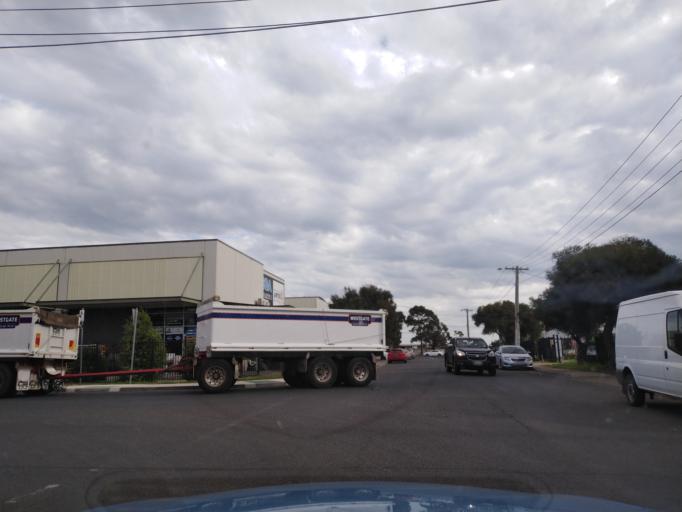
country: AU
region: Victoria
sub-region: Hobsons Bay
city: Williamstown North
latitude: -37.8542
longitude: 144.8652
